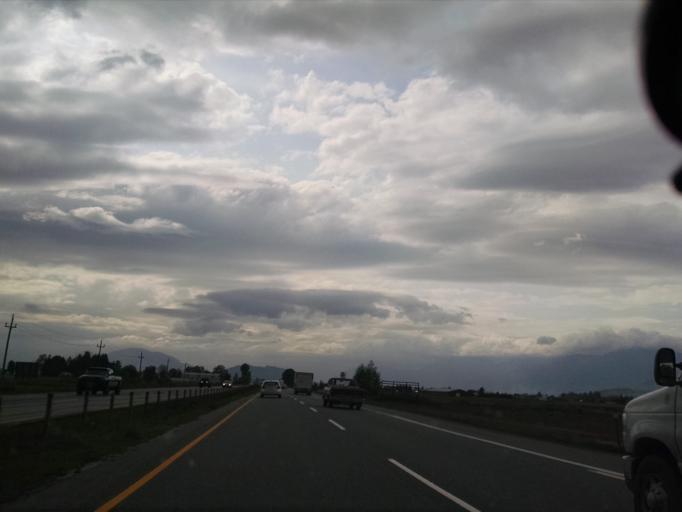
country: CA
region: British Columbia
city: Agassiz
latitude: 49.1549
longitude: -121.8387
